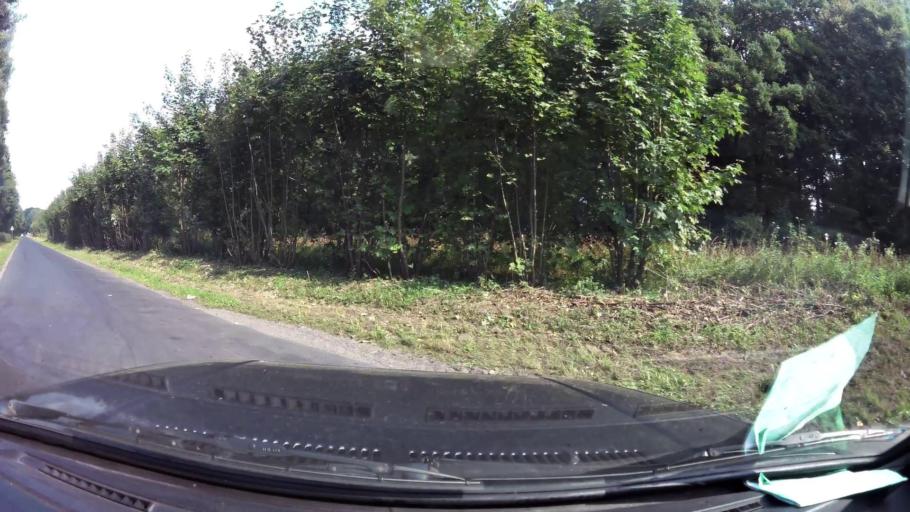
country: PL
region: West Pomeranian Voivodeship
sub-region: Powiat koszalinski
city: Polanow
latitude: 54.1336
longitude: 16.5241
